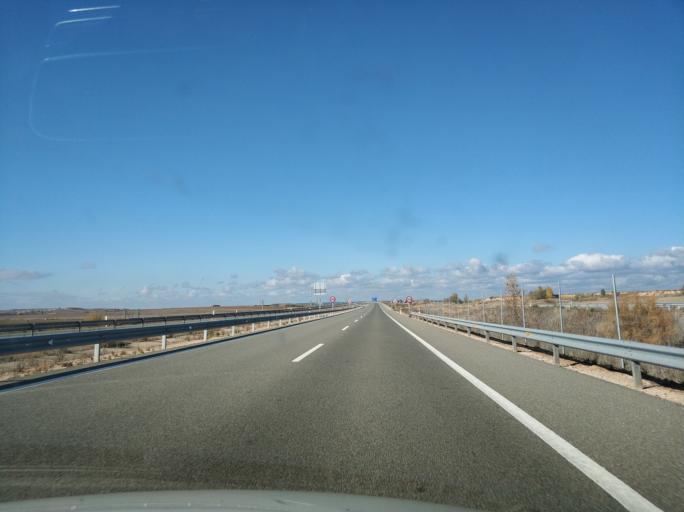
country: ES
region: Castille and Leon
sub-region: Provincia de Soria
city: Frechilla de Almazan
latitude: 41.4529
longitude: -2.5122
